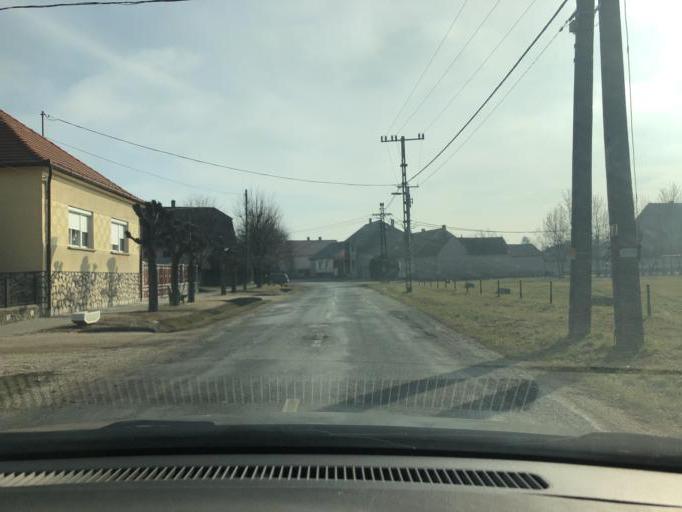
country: HU
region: Gyor-Moson-Sopron
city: Kapuvar
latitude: 47.6022
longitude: 17.0836
